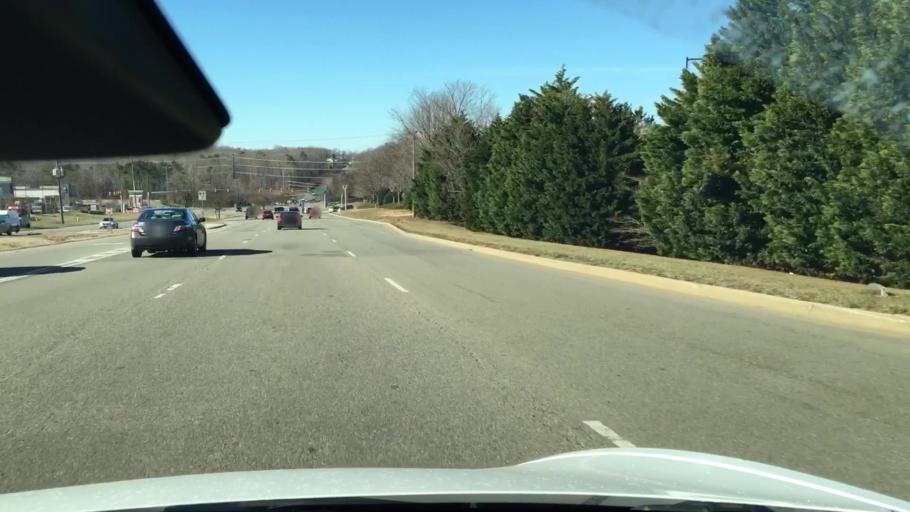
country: US
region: Virginia
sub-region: Chesterfield County
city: Bon Air
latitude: 37.5041
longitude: -77.6251
